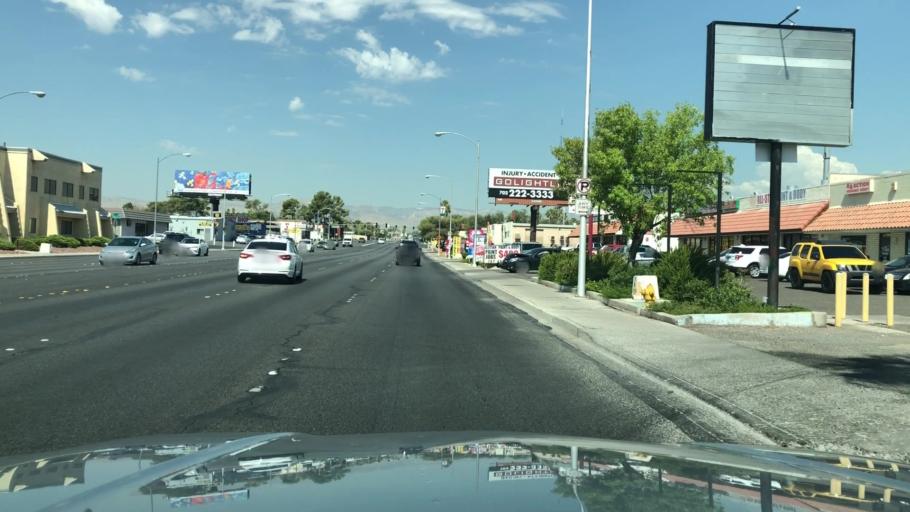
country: US
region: Nevada
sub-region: Clark County
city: Spring Valley
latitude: 36.1302
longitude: -115.1959
